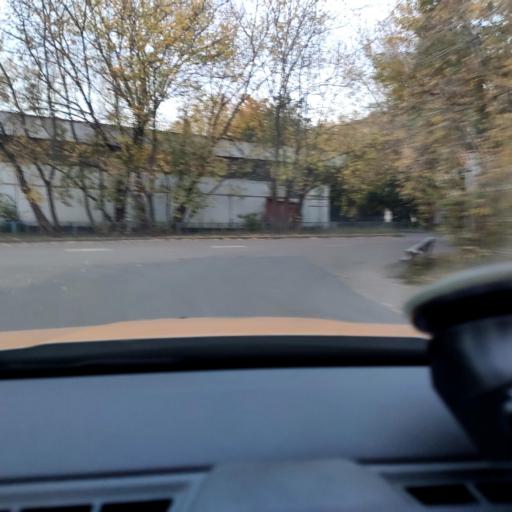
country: RU
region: Moscow
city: Yaroslavskiy
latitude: 55.8638
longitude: 37.7039
